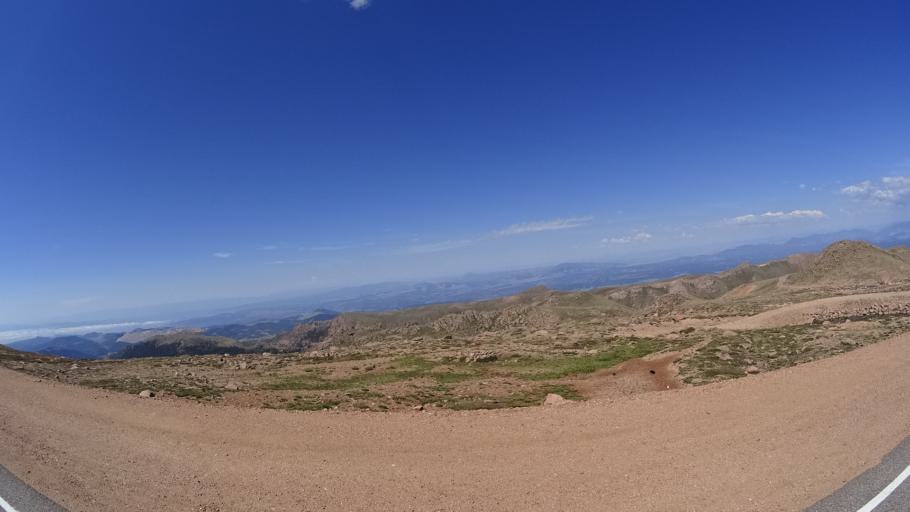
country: US
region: Colorado
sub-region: El Paso County
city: Cascade-Chipita Park
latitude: 38.8440
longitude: -105.0503
